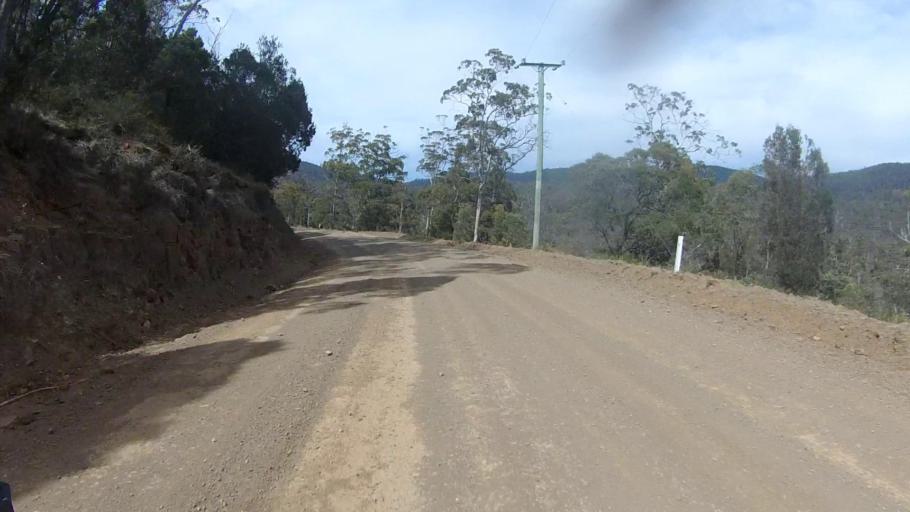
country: AU
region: Tasmania
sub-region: Sorell
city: Sorell
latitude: -42.6695
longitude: 147.8842
